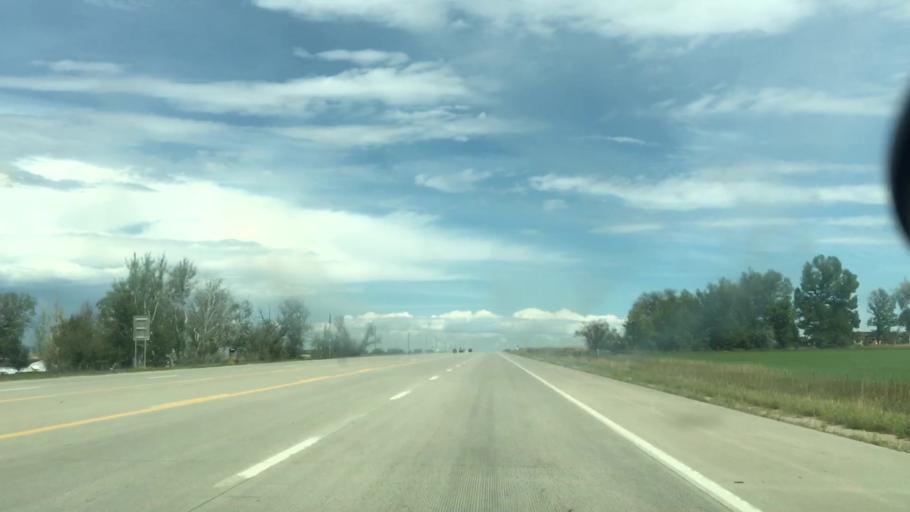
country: US
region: Colorado
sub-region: Boulder County
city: Longmont
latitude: 40.2130
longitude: -105.1023
